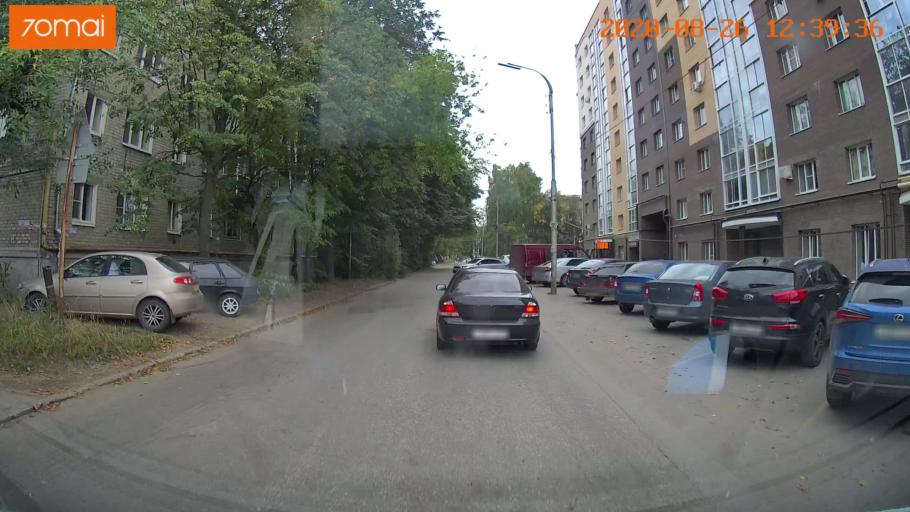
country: RU
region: Rjazan
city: Ryazan'
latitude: 54.6050
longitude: 39.7583
